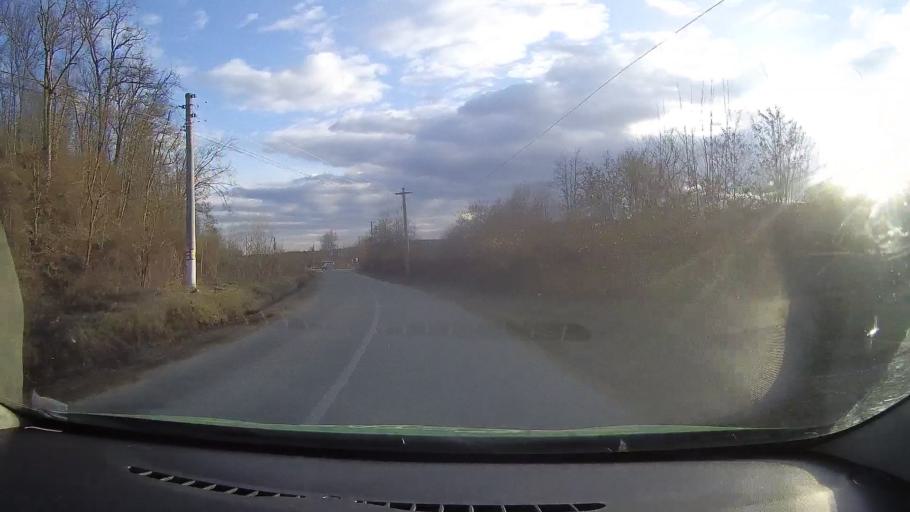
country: RO
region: Dambovita
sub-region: Comuna Ocnita
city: Ocnita
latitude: 44.9660
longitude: 25.5473
